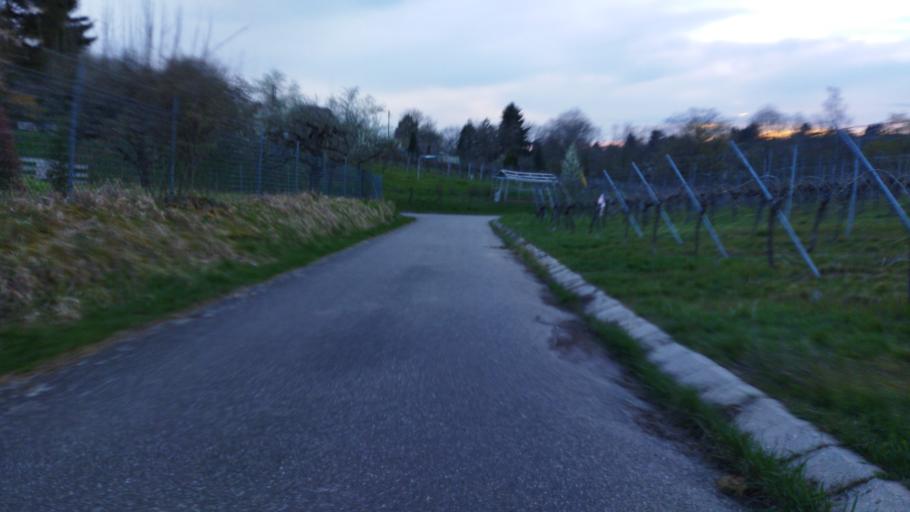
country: DE
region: Baden-Wuerttemberg
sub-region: Regierungsbezirk Stuttgart
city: Weinsberg
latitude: 49.1425
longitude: 9.2598
